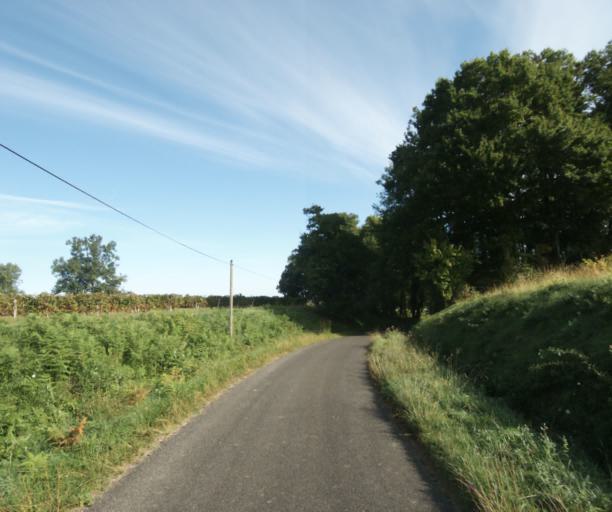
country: FR
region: Midi-Pyrenees
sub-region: Departement du Gers
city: Eauze
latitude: 43.9359
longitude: 0.1182
